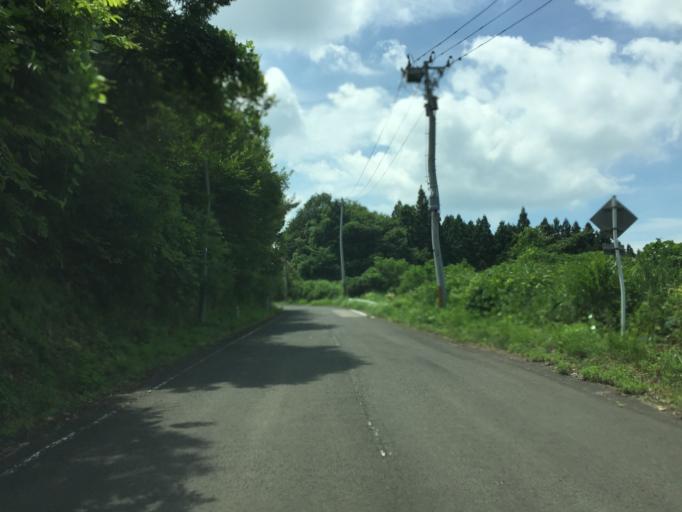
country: JP
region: Fukushima
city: Funehikimachi-funehiki
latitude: 37.6316
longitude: 140.6625
